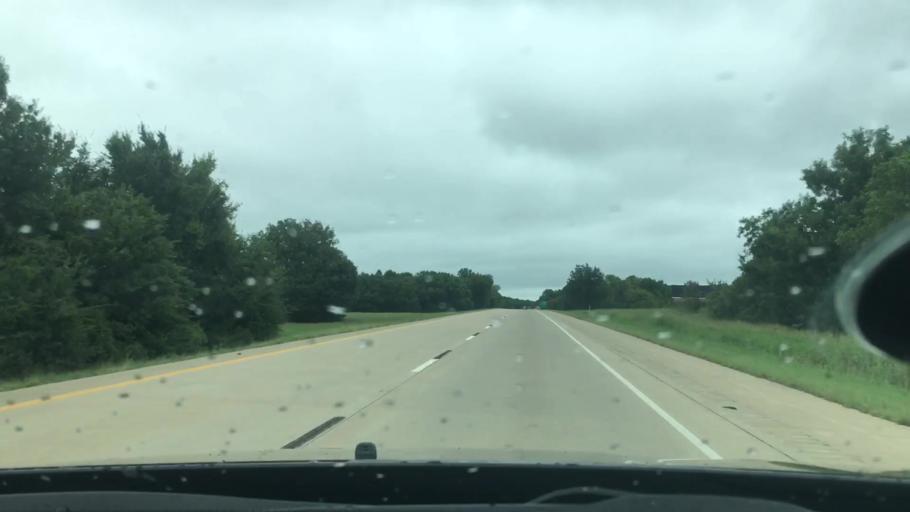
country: US
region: Oklahoma
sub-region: Okmulgee County
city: Morris
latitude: 35.4505
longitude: -95.7294
